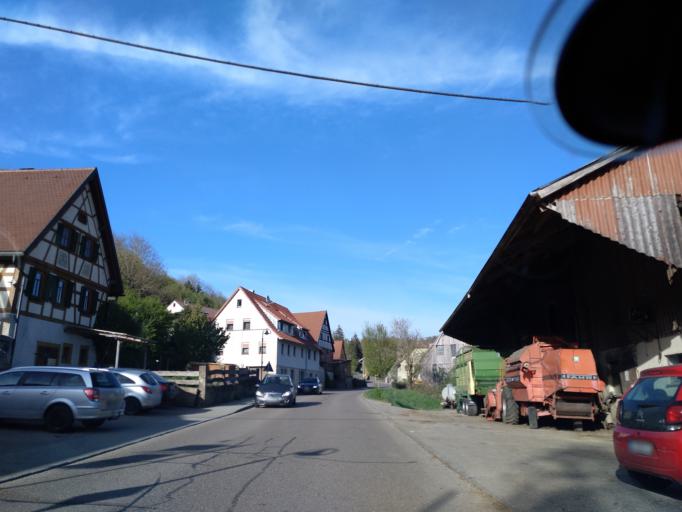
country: DE
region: Baden-Wuerttemberg
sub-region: Regierungsbezirk Stuttgart
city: Langenburg
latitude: 49.2226
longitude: 9.9003
